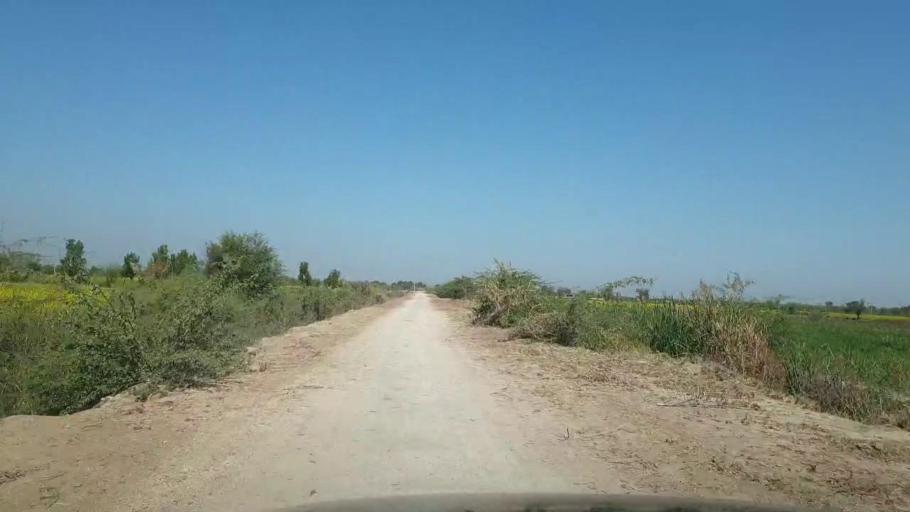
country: PK
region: Sindh
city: Mirpur Khas
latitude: 25.5934
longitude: 69.0683
